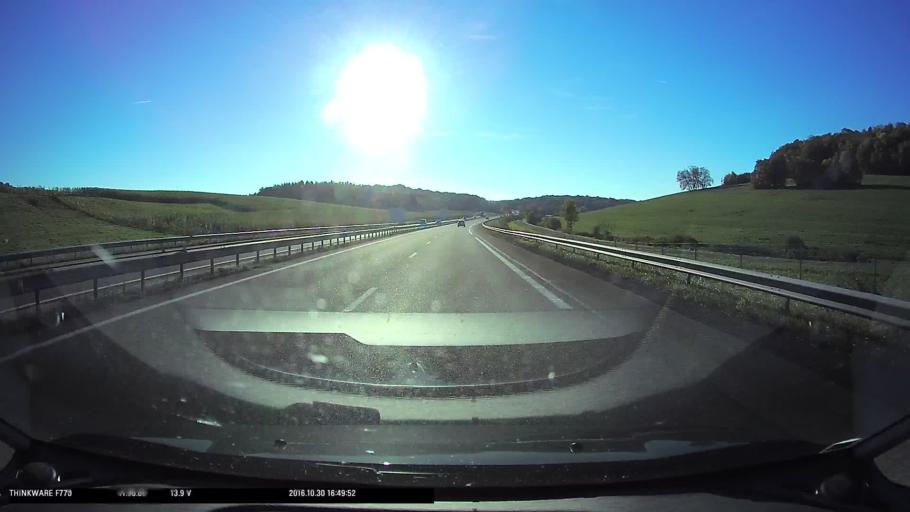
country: FR
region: Franche-Comte
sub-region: Departement du Doubs
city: Pouilley-les-Vignes
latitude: 47.2754
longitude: 5.9429
